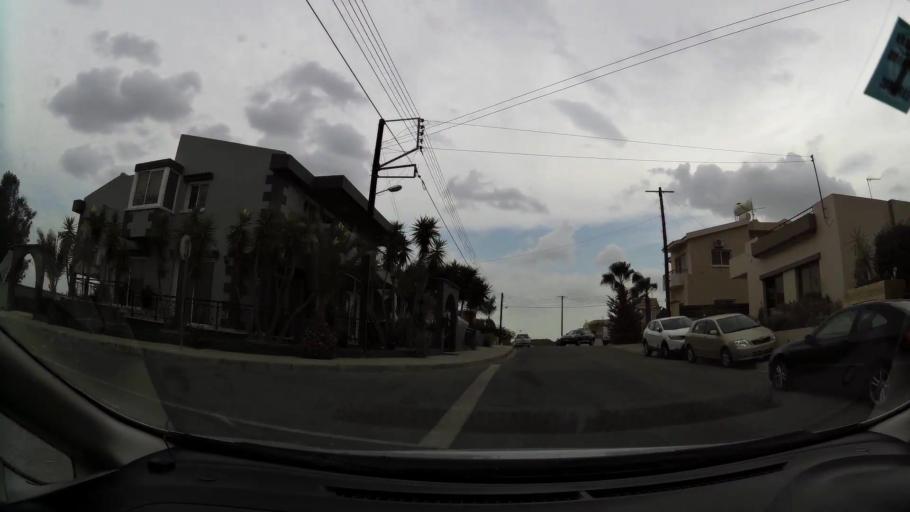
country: CY
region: Lefkosia
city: Geri
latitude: 35.0993
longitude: 33.3940
